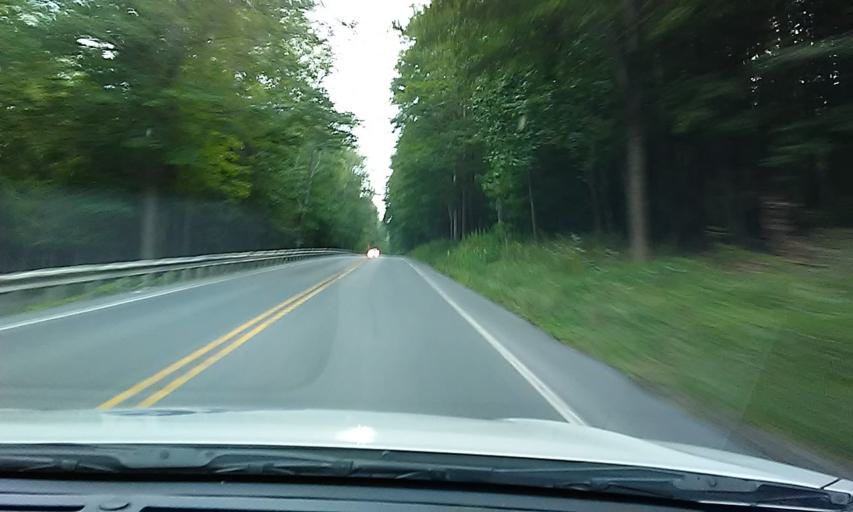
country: US
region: Pennsylvania
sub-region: McKean County
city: Kane
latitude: 41.5940
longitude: -78.8420
